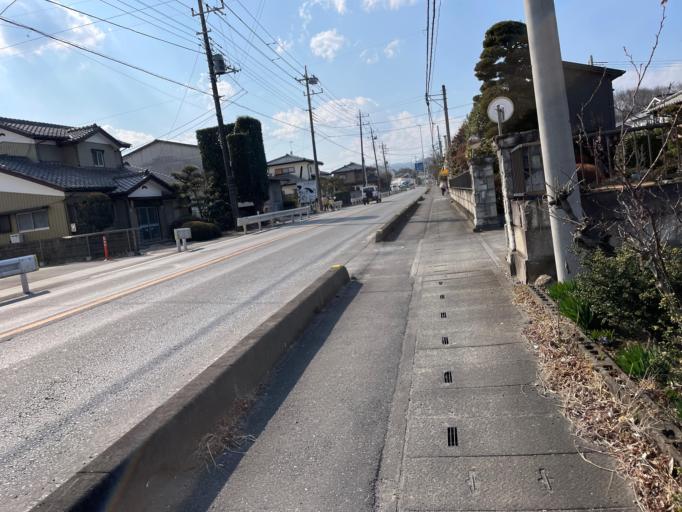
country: JP
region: Saitama
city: Yorii
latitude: 36.1260
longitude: 139.2246
